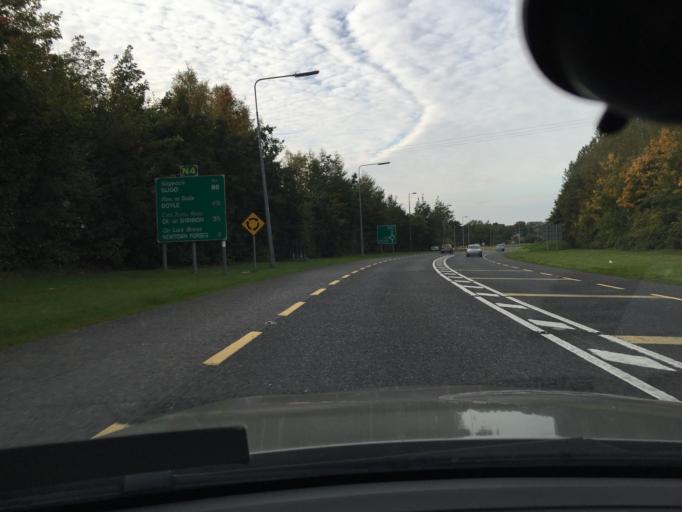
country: IE
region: Leinster
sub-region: An Longfort
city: Longford
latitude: 53.7424
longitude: -7.8050
